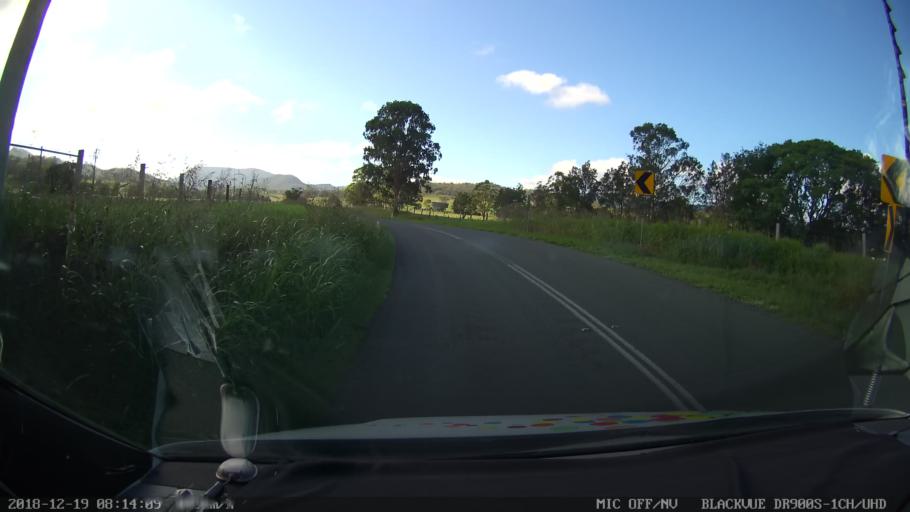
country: AU
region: Queensland
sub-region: Logan
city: Cedar Vale
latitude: -28.2455
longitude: 152.8901
